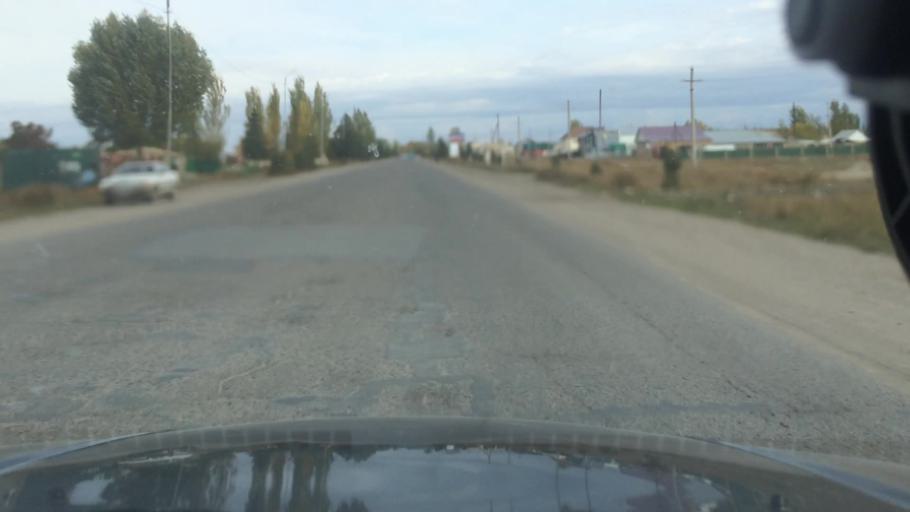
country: KG
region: Ysyk-Koel
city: Karakol
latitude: 42.5234
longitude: 78.3859
